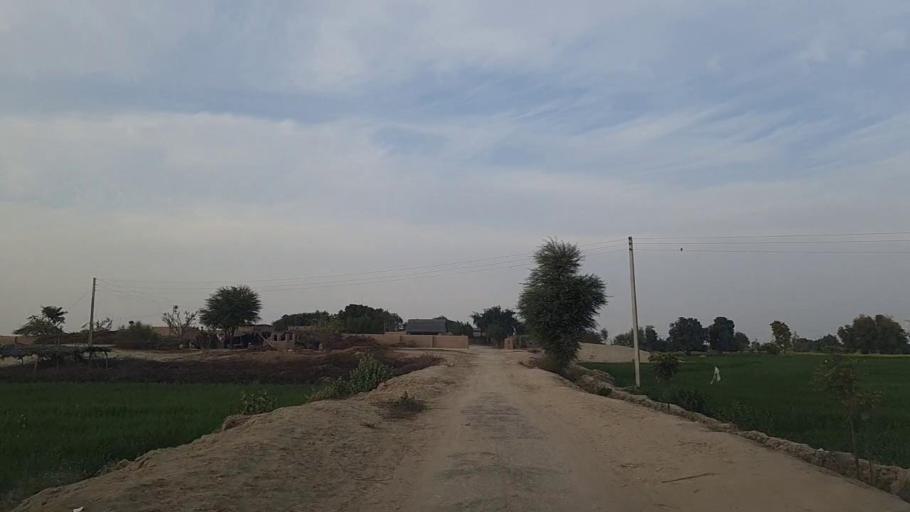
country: PK
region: Sindh
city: Jam Sahib
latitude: 26.4654
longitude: 68.5622
